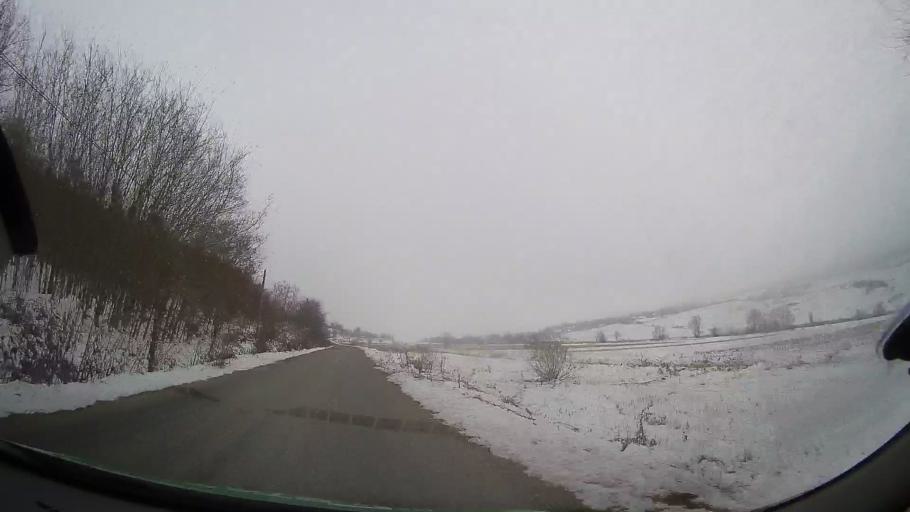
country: RO
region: Bacau
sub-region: Comuna Vultureni
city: Vultureni
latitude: 46.3373
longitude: 27.2906
